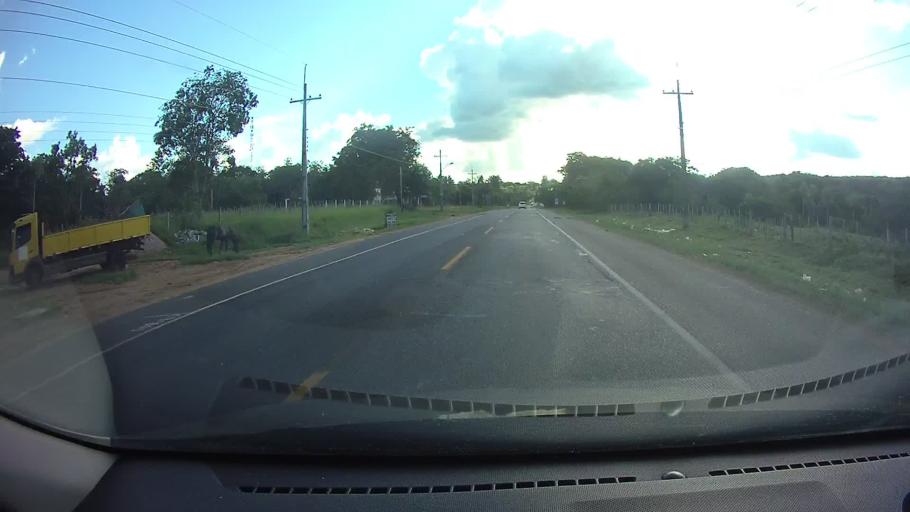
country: PY
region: Cordillera
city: Eusebio Ayala
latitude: -25.3792
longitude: -57.0366
